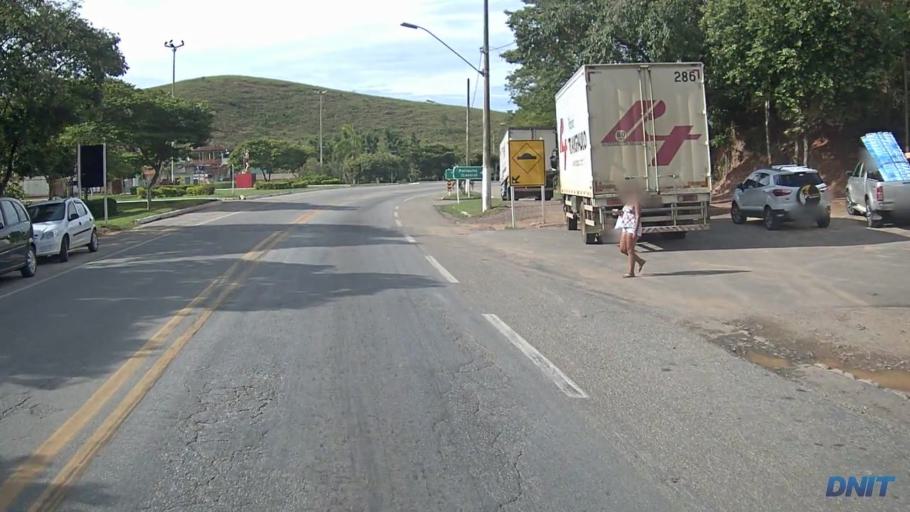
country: BR
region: Minas Gerais
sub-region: Belo Oriente
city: Belo Oriente
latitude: -19.1578
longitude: -42.2377
